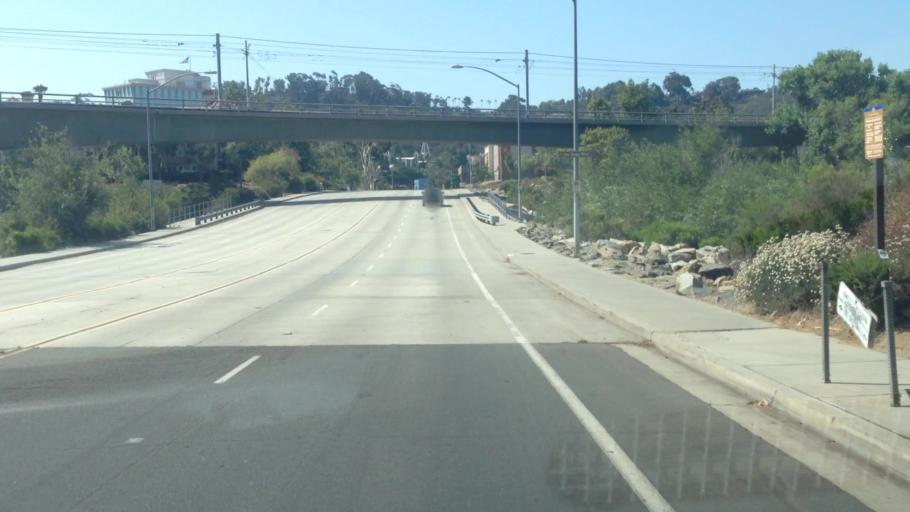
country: US
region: California
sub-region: San Diego County
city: San Diego
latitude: 32.7733
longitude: -117.1450
